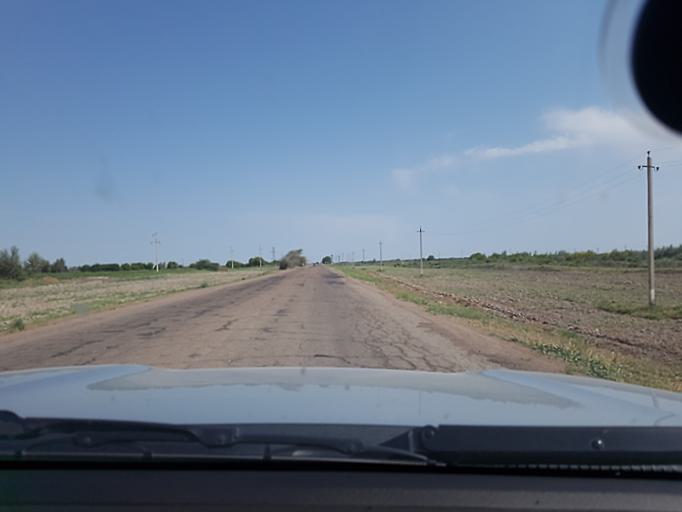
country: UZ
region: Karakalpakstan
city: Khujayli
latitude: 42.2335
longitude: 59.4578
